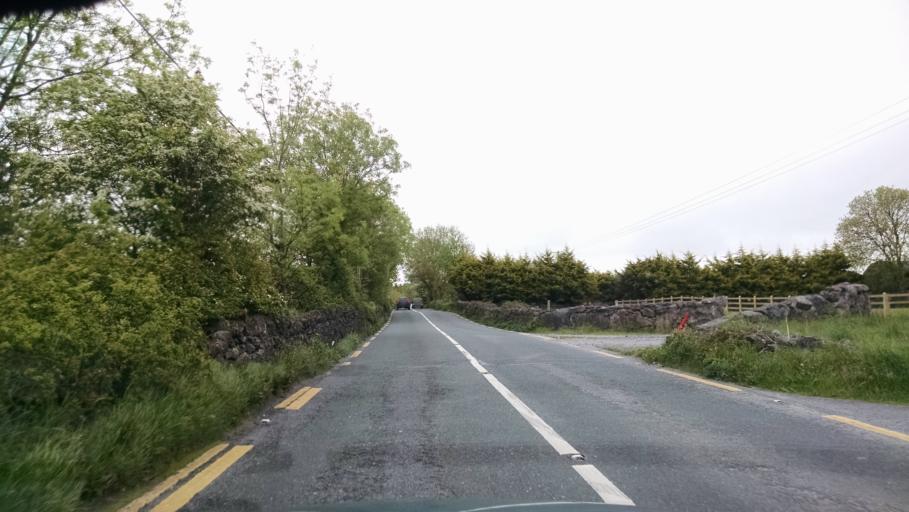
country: IE
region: Connaught
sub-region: County Galway
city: Moycullen
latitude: 53.4419
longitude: -9.0795
